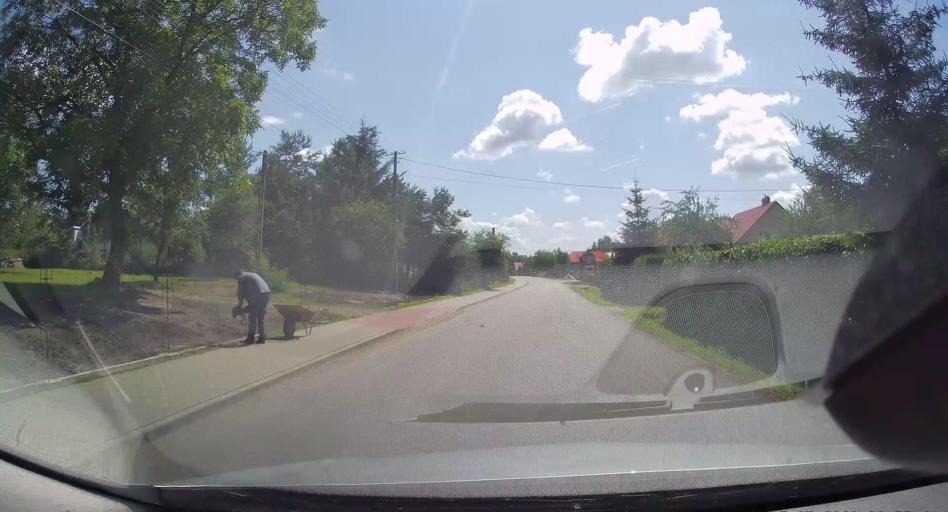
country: PL
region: Subcarpathian Voivodeship
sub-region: Powiat jaroslawski
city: Sosnica
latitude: 49.8647
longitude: 22.8768
